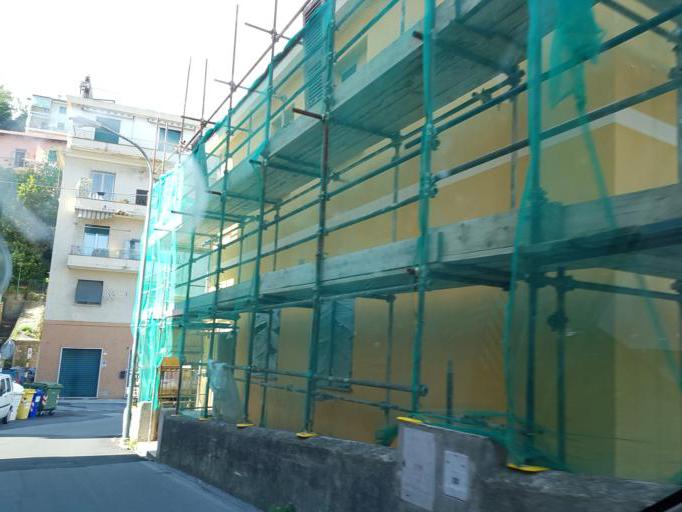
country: IT
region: Liguria
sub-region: Provincia di Genova
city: Genoa
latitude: 44.4581
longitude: 8.8967
